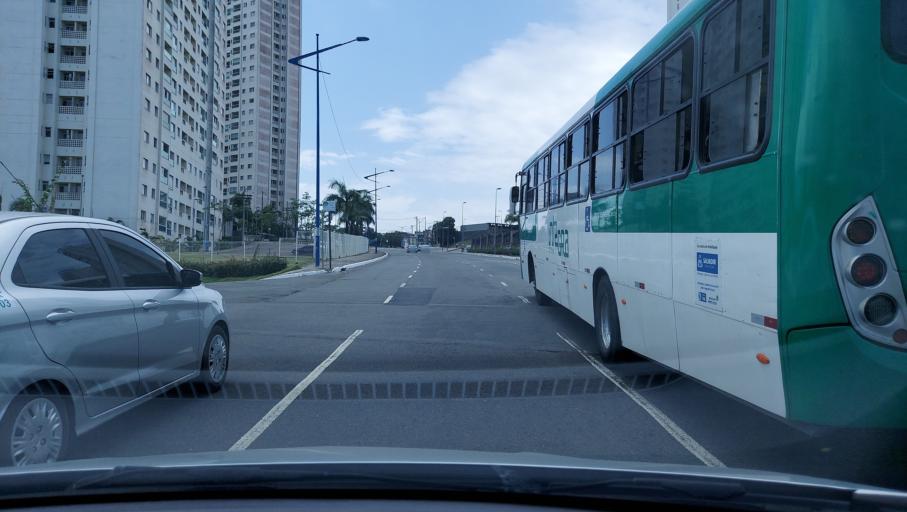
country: BR
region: Bahia
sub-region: Salvador
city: Salvador
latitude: -12.9672
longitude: -38.4755
